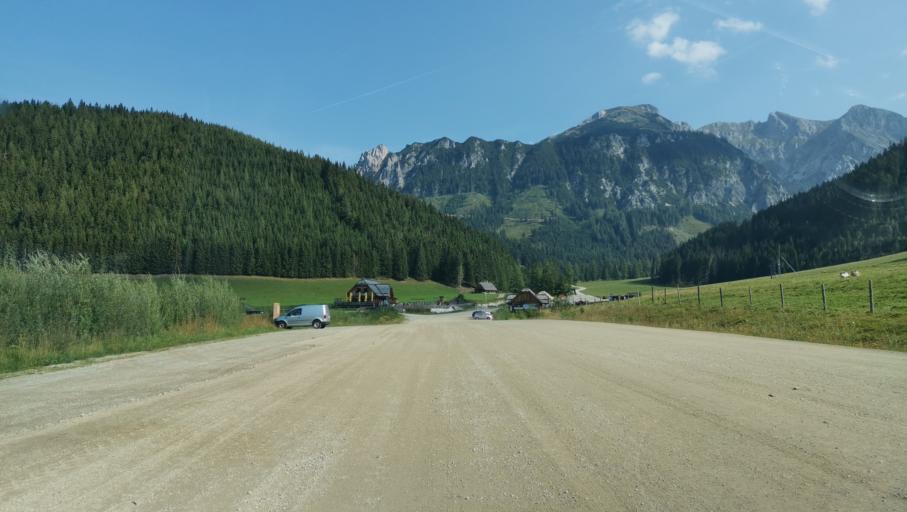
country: AT
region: Styria
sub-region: Politischer Bezirk Liezen
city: Trieben
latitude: 47.5274
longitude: 14.4842
